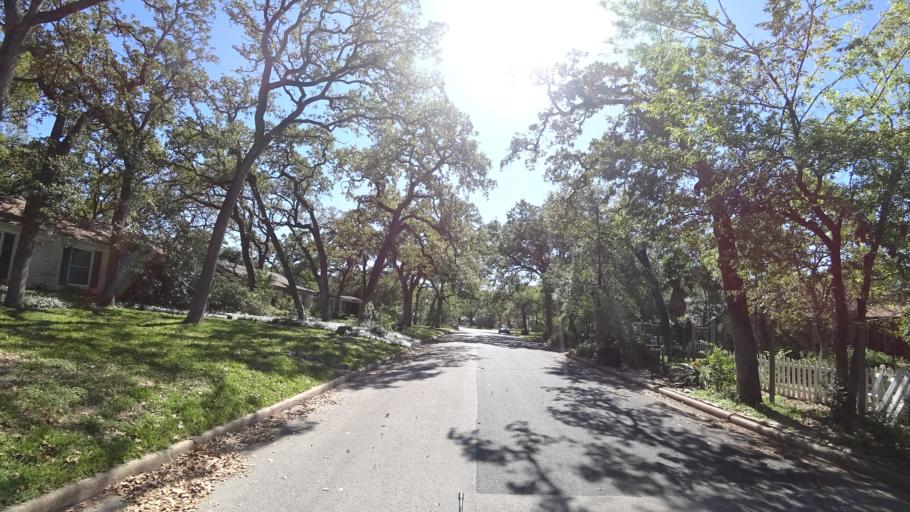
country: US
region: Texas
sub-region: Travis County
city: Austin
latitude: 30.2982
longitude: -97.7161
